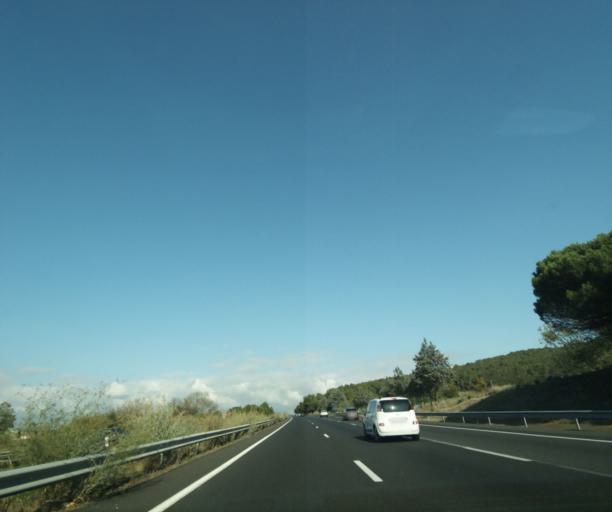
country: FR
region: Languedoc-Roussillon
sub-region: Departement de l'Aude
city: Vinassan
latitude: 43.1982
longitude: 3.0772
